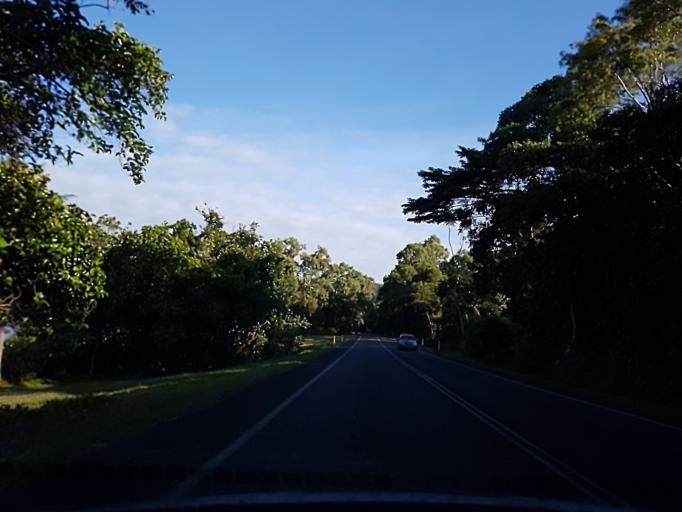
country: AU
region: Queensland
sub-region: Cairns
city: Port Douglas
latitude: -16.3699
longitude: 145.4117
